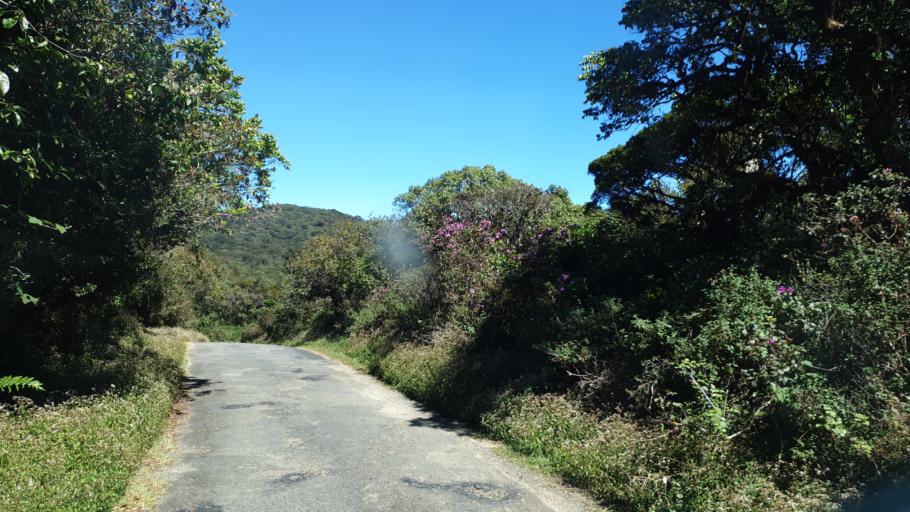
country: LK
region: Central
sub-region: Nuwara Eliya District
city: Nuwara Eliya
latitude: 6.8272
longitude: 80.8064
